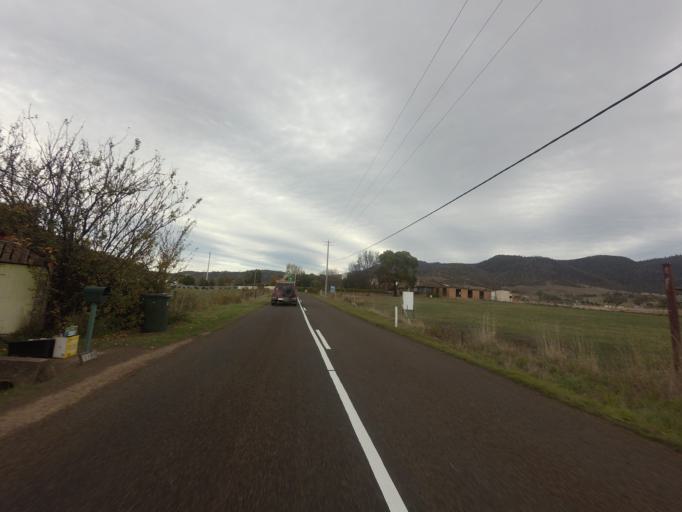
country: AU
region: Tasmania
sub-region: Brighton
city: Bridgewater
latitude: -42.6591
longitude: 147.1267
